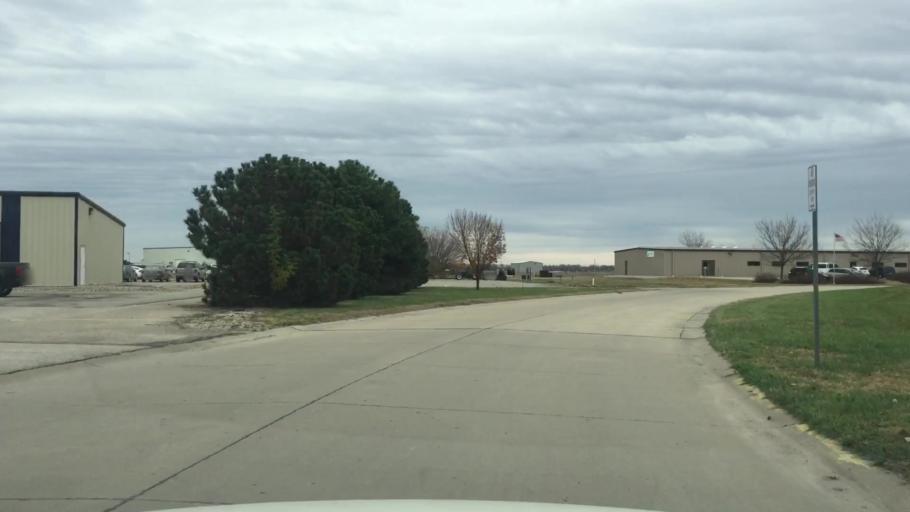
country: US
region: Kansas
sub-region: Pottawatomie County
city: Wamego
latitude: 39.2088
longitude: -96.2881
